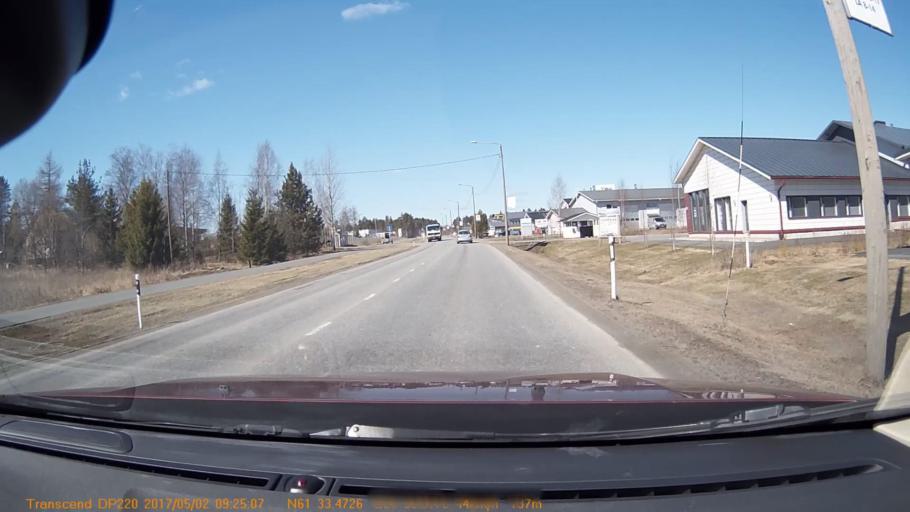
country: FI
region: Pirkanmaa
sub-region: Tampere
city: Yloejaervi
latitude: 61.5579
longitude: 23.5583
